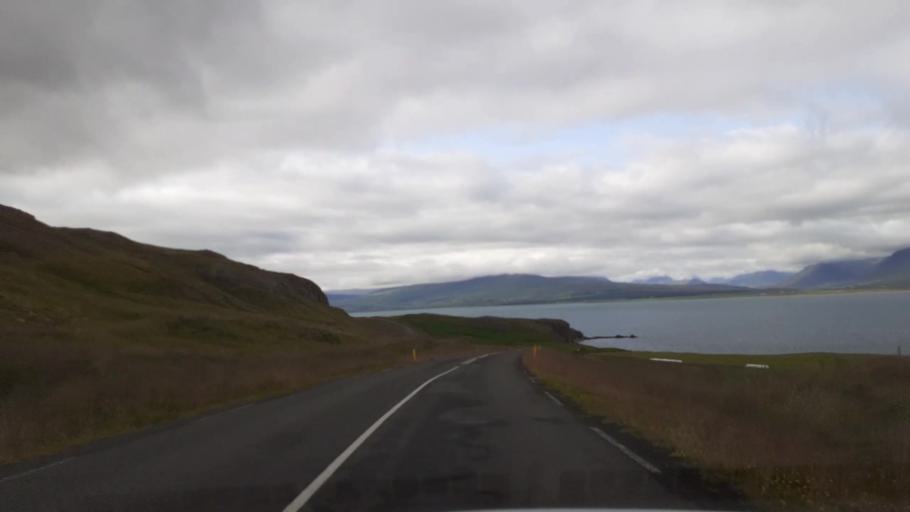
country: IS
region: Northeast
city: Akureyri
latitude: 65.8144
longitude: -18.0495
